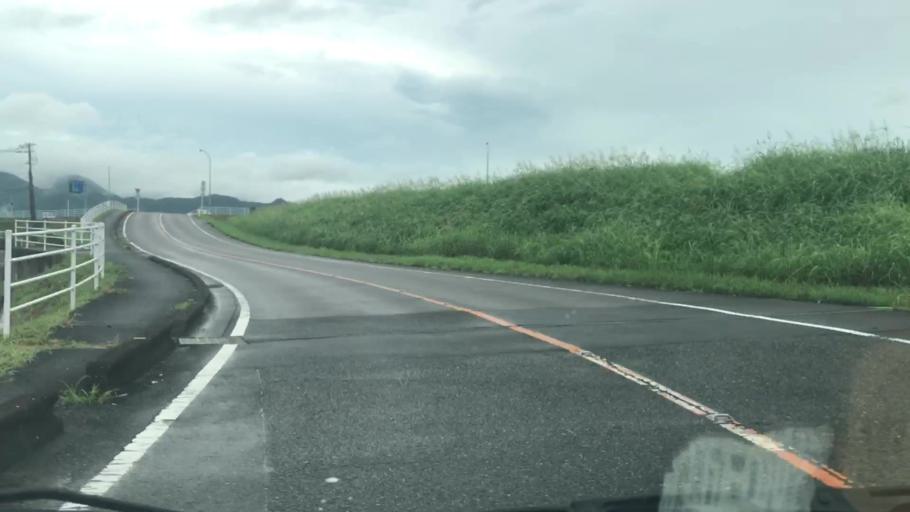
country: JP
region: Saga Prefecture
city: Takeocho-takeo
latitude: 33.2006
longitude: 130.0527
